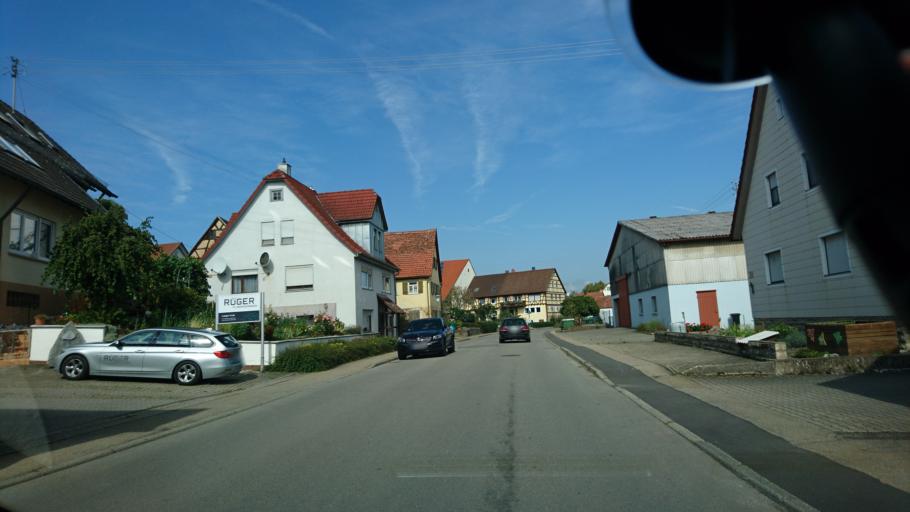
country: DE
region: Baden-Wuerttemberg
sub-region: Regierungsbezirk Stuttgart
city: Ilshofen
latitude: 49.1532
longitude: 9.9306
